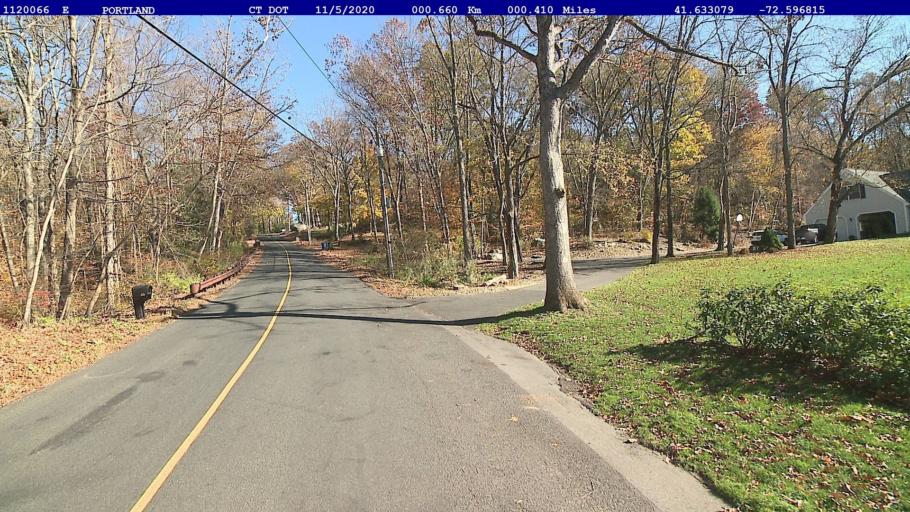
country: US
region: Connecticut
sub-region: Middlesex County
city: Cromwell
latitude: 41.6331
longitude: -72.5968
